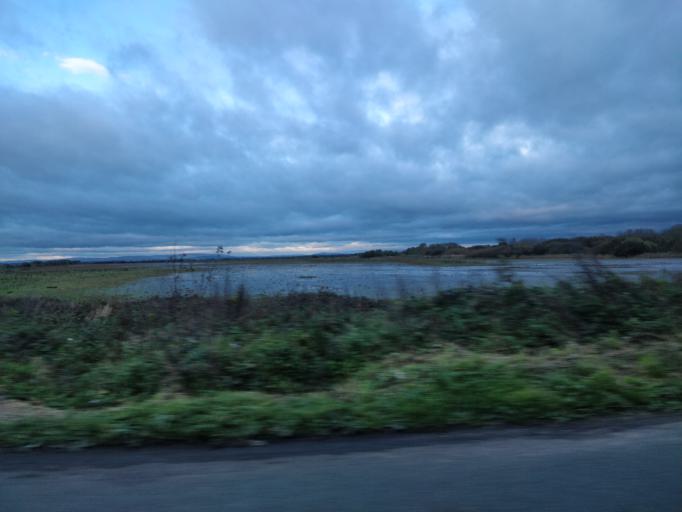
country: GB
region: England
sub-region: Sefton
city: Southport
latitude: 53.6664
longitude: -2.9920
